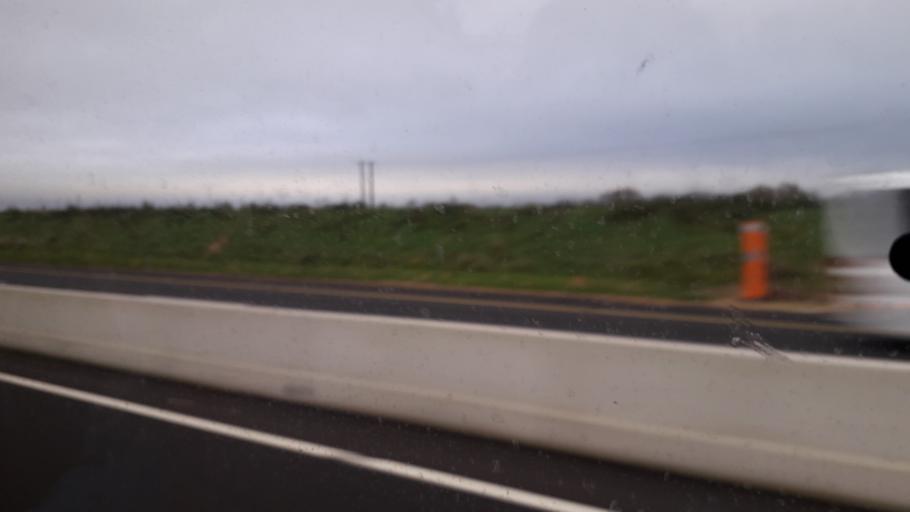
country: IE
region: Connaught
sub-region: County Galway
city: Athenry
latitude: 53.2712
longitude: -8.8066
